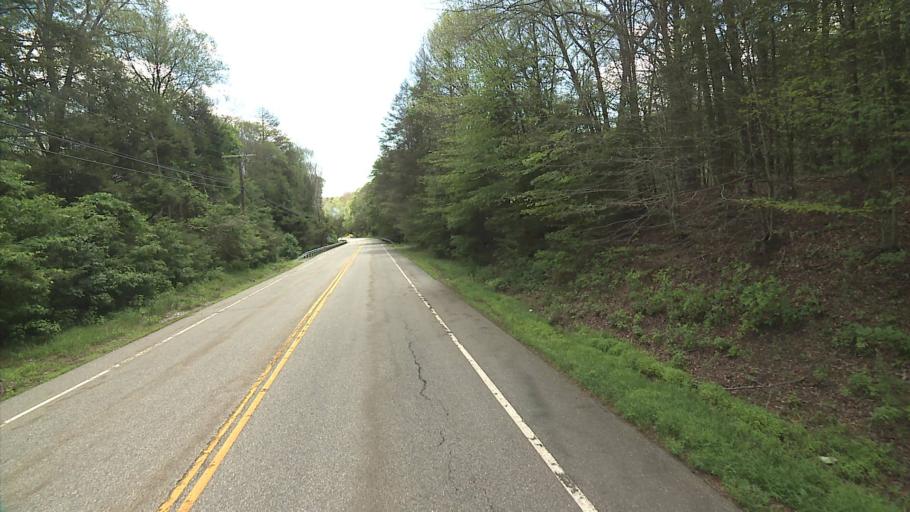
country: US
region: Connecticut
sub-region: Middlesex County
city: Moodus
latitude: 41.5188
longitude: -72.5024
